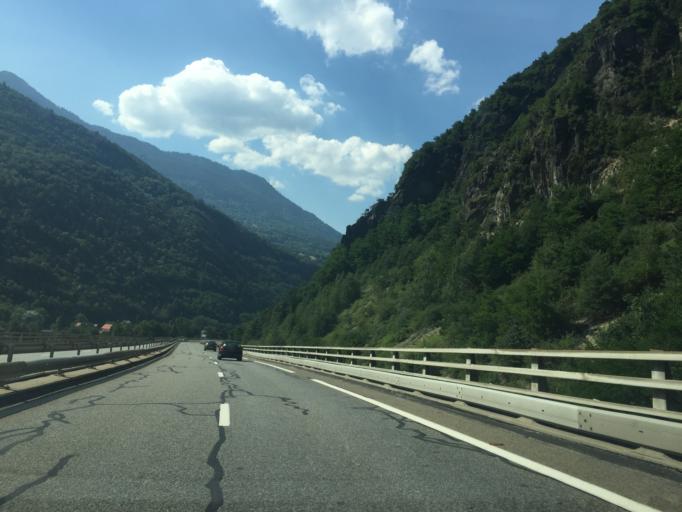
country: FR
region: Rhone-Alpes
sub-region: Departement de la Savoie
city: Aigueblanche
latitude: 45.5347
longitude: 6.4737
